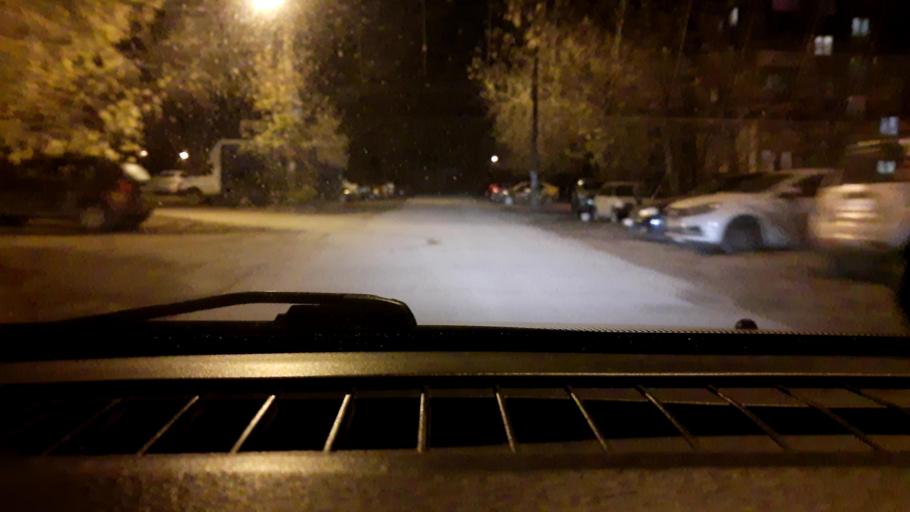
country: RU
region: Nizjnij Novgorod
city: Gorbatovka
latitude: 56.3581
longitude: 43.8368
